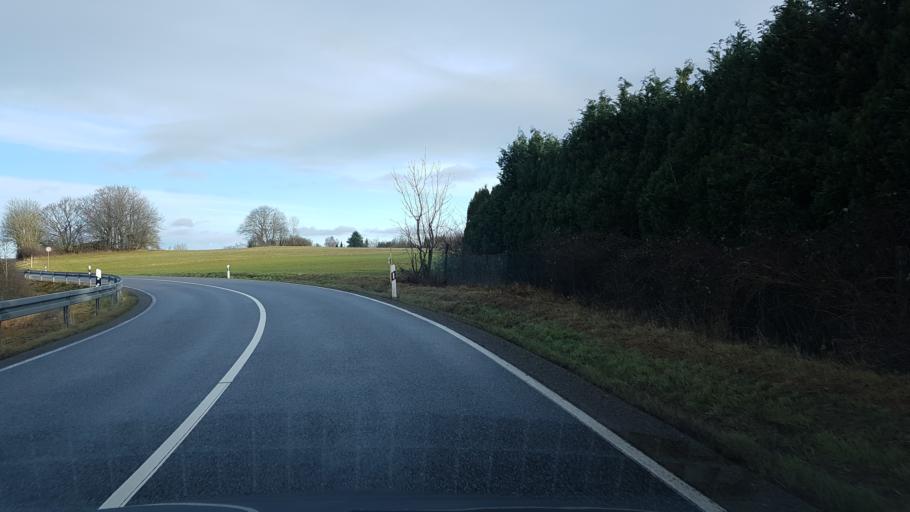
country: DE
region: Saarland
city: Sankt Ingbert
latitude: 49.2352
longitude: 7.1263
